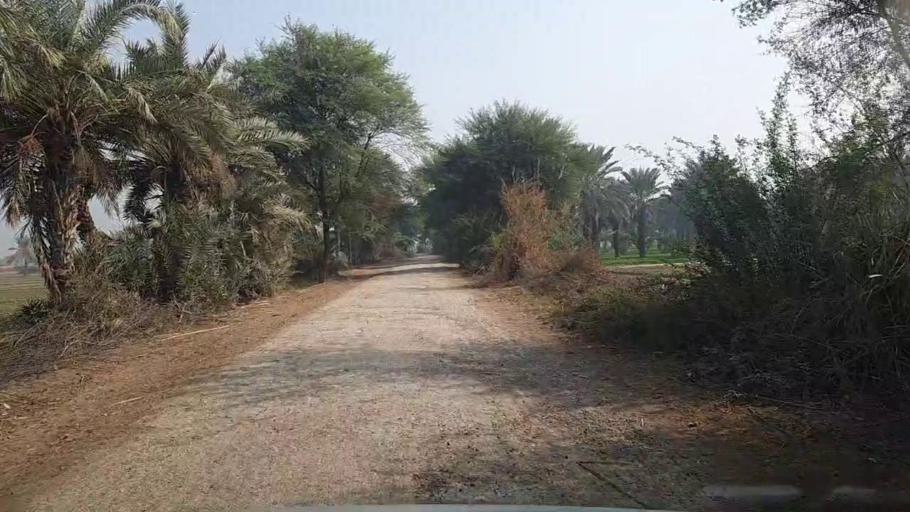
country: PK
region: Sindh
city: Setharja Old
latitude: 27.1388
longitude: 68.5070
